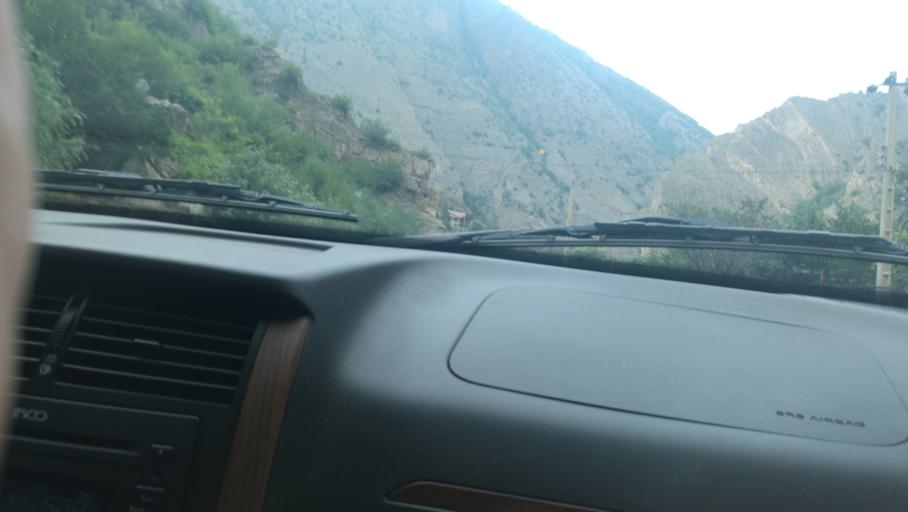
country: IR
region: Mazandaran
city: Chalus
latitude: 36.3122
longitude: 51.2481
